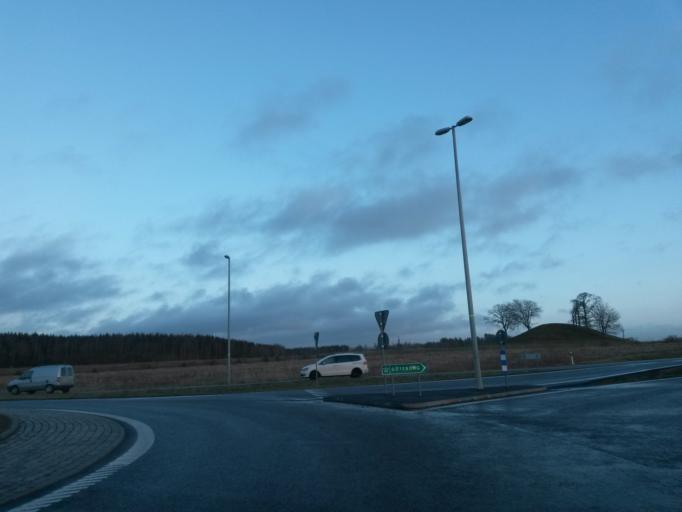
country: SE
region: Halland
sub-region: Halmstads Kommun
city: Halmstad
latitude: 56.7113
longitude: 12.8900
